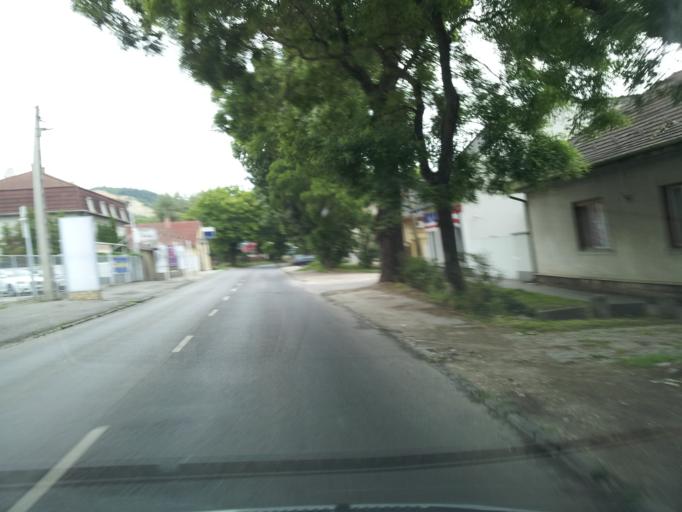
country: HU
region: Pest
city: Urom
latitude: 47.5838
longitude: 19.0453
